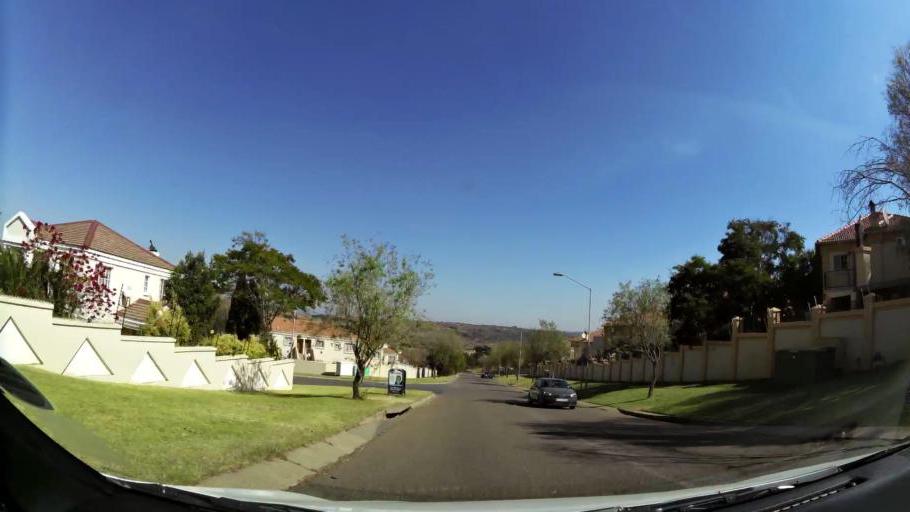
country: ZA
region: Gauteng
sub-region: City of Tshwane Metropolitan Municipality
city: Pretoria
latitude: -25.7940
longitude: 28.2293
